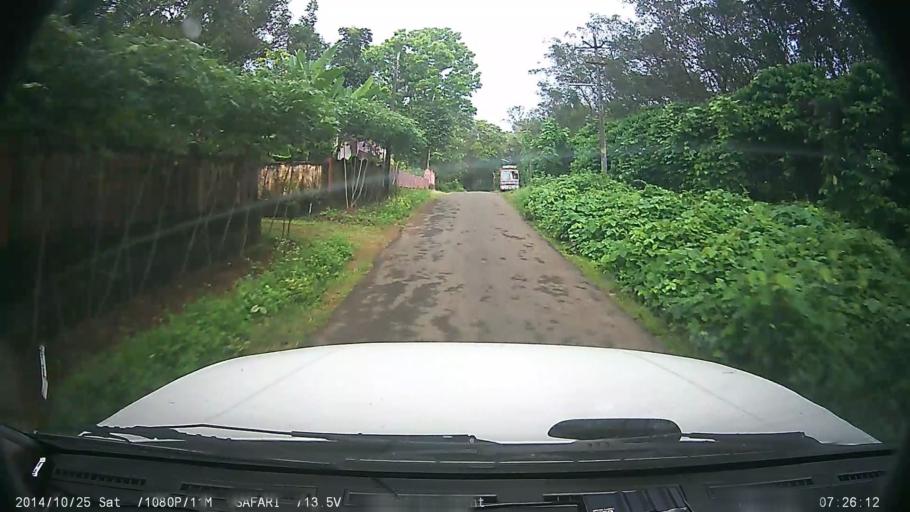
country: IN
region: Kerala
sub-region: Kottayam
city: Palackattumala
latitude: 9.7811
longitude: 76.5744
